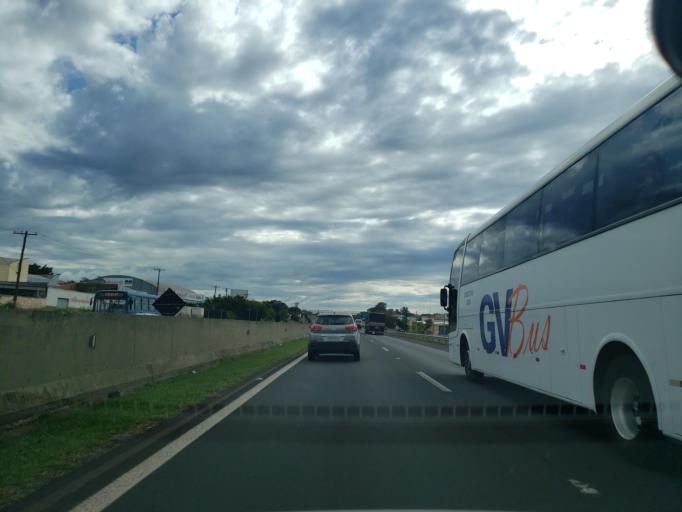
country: BR
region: Sao Paulo
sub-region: Bauru
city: Bauru
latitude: -22.3002
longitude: -49.0653
